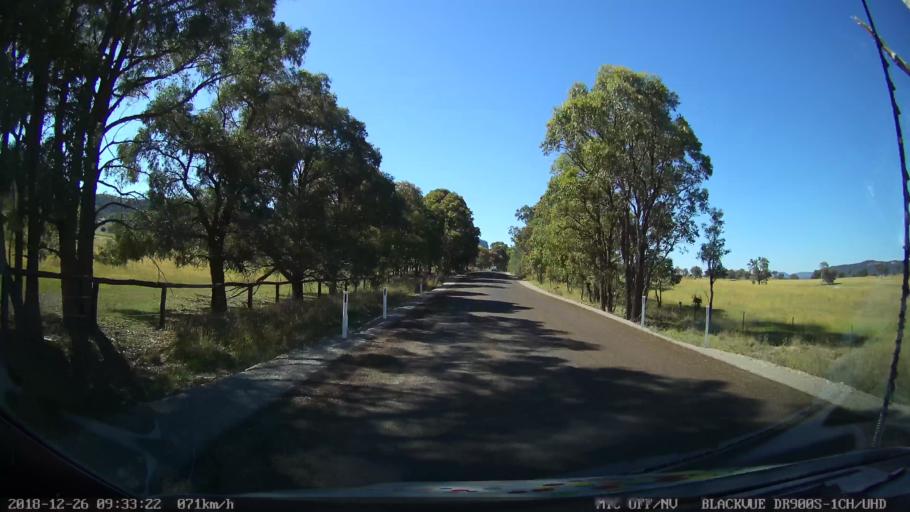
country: AU
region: New South Wales
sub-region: Mid-Western Regional
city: Kandos
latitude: -32.8940
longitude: 150.0347
